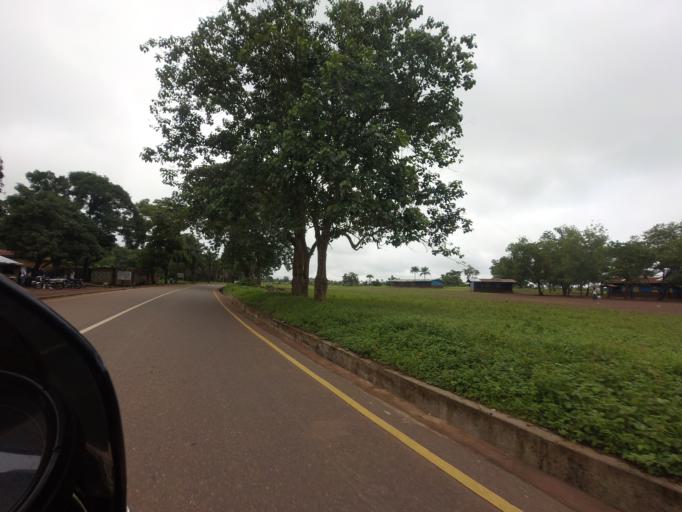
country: SL
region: Northern Province
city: Kambia
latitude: 9.1282
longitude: -12.9076
